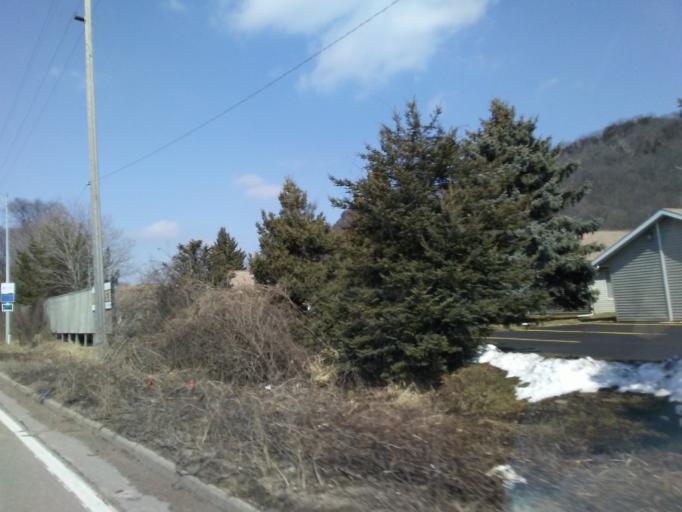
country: US
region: Wisconsin
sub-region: La Crosse County
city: La Crosse
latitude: 43.7581
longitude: -91.2050
